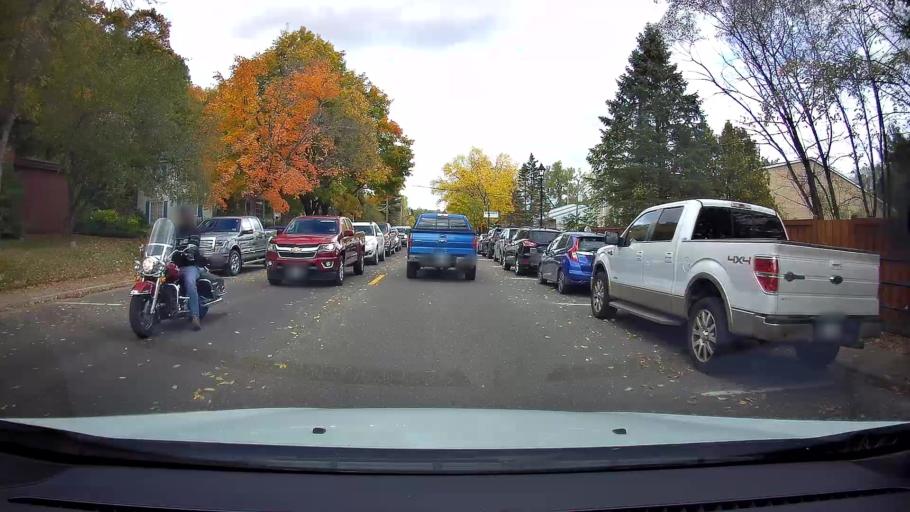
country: US
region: Wisconsin
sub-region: Polk County
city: Saint Croix Falls
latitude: 45.4041
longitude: -92.6526
